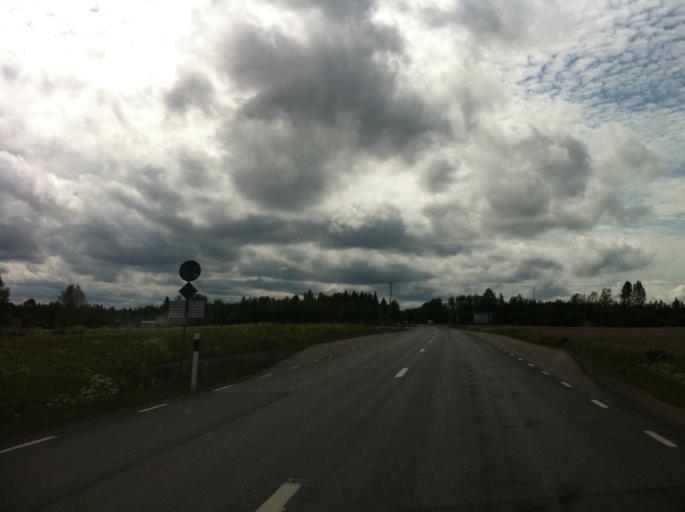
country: SE
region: Vaermland
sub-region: Sunne Kommun
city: Sunne
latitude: 59.7187
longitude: 13.1373
